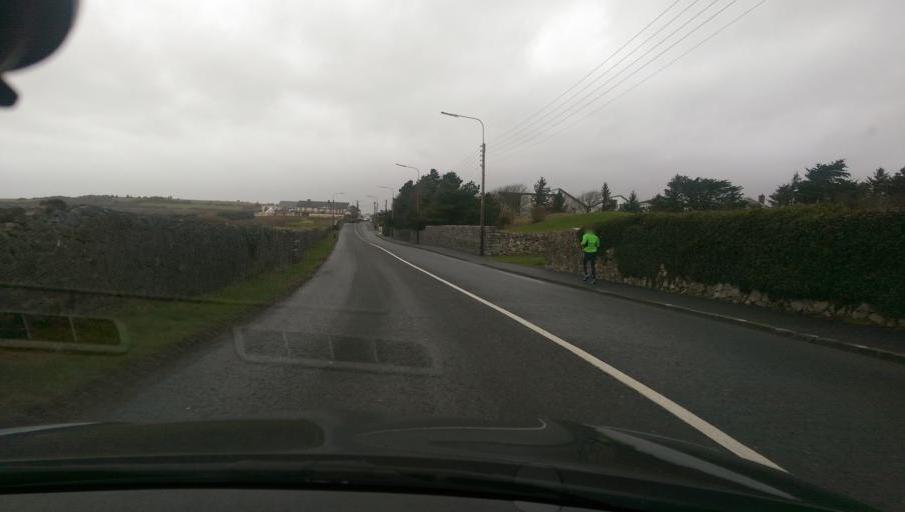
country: IE
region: Connaught
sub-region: County Galway
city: Gaillimh
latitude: 53.2584
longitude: -9.0969
